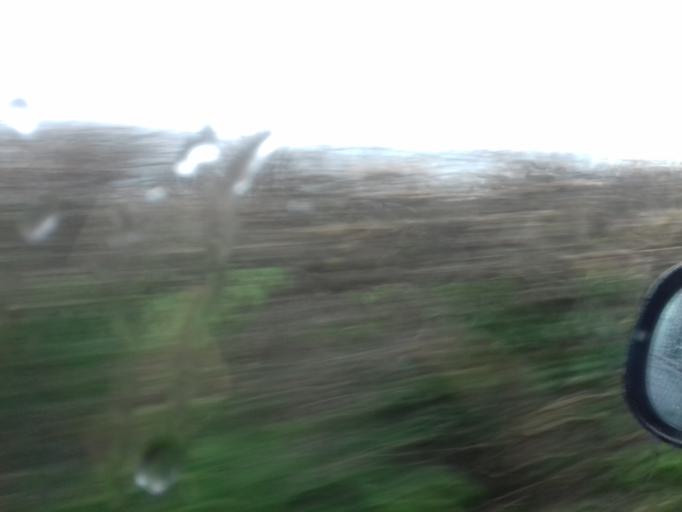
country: IE
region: Leinster
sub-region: Kilkenny
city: Graiguenamanagh
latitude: 52.5923
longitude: -7.0025
